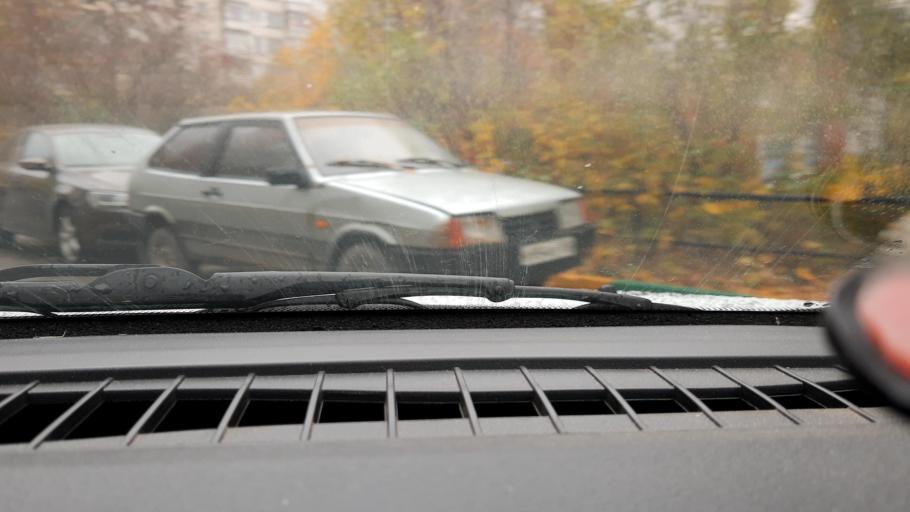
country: RU
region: Nizjnij Novgorod
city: Nizhniy Novgorod
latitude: 56.2964
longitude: 43.9939
